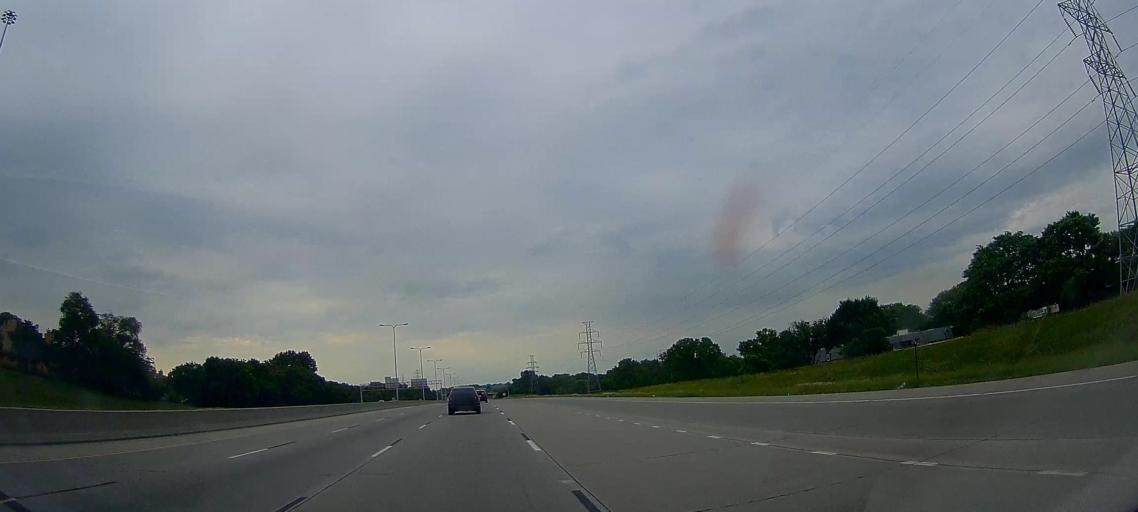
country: US
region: Nebraska
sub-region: Douglas County
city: Ralston
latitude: 41.2895
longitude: -96.0743
